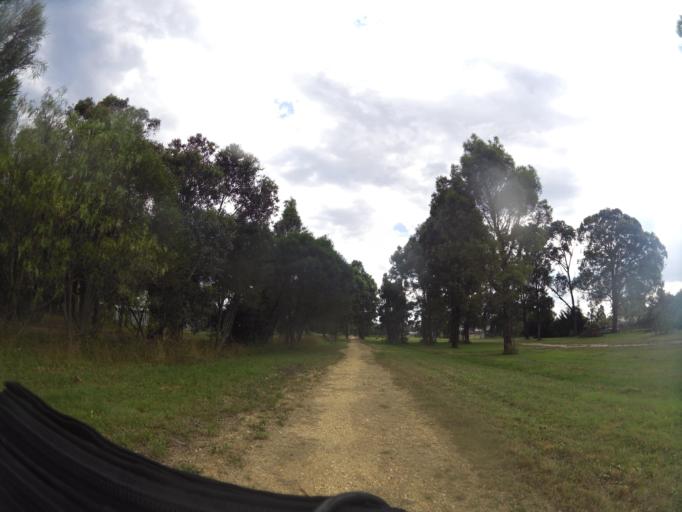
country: AU
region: Victoria
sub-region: Latrobe
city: Traralgon
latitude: -38.0541
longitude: 146.6278
